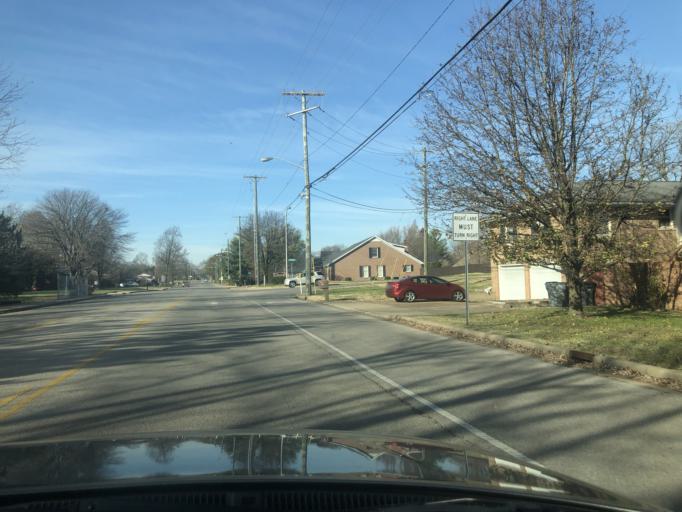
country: US
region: Indiana
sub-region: Warrick County
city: Newburgh
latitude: 37.9695
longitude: -87.4587
